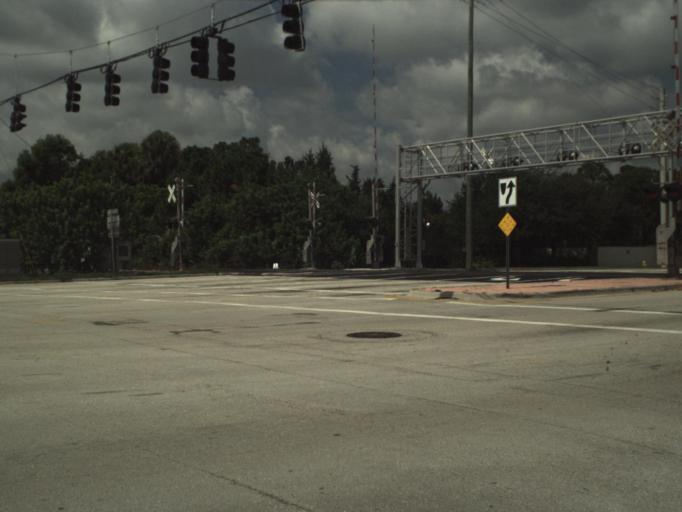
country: US
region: Florida
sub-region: Palm Beach County
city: Juno Beach
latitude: 26.8830
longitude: -80.0953
